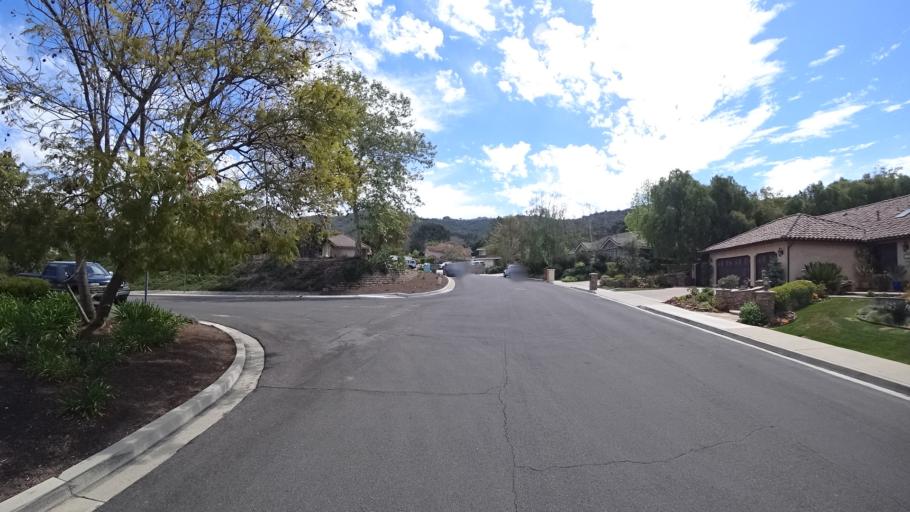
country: US
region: California
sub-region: Ventura County
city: Casa Conejo
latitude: 34.1600
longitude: -118.9432
